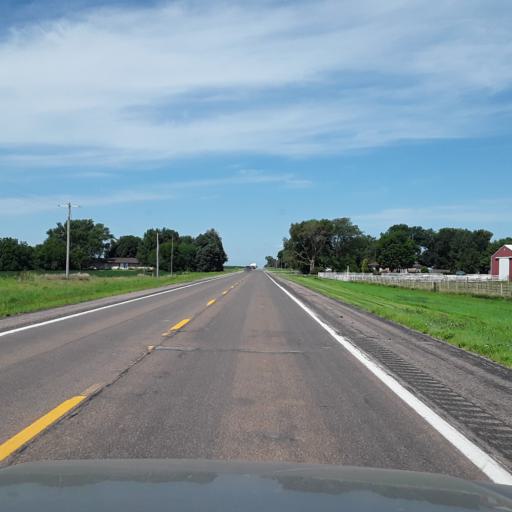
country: US
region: Nebraska
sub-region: Seward County
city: Seward
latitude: 40.9016
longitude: -97.1736
